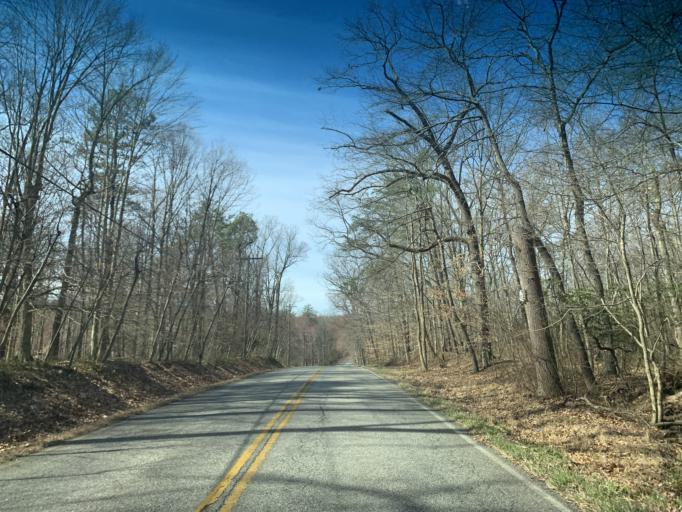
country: US
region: Maryland
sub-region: Cecil County
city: Charlestown
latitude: 39.5684
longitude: -75.9926
